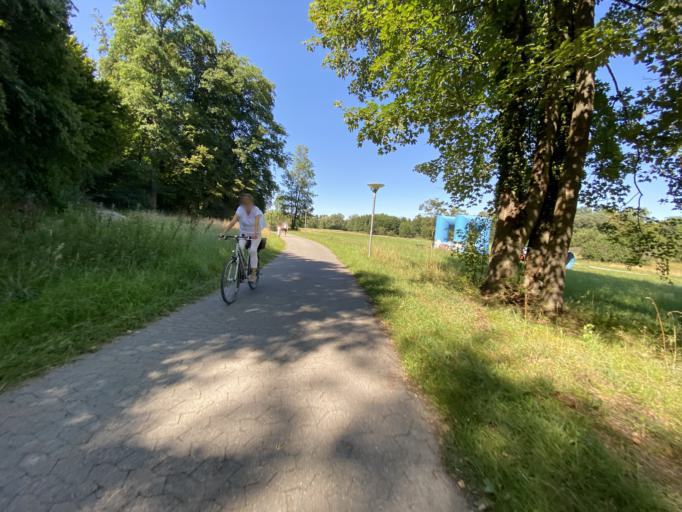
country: DE
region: Baden-Wuerttemberg
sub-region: Freiburg Region
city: Konstanz
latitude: 47.6837
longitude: 9.1896
